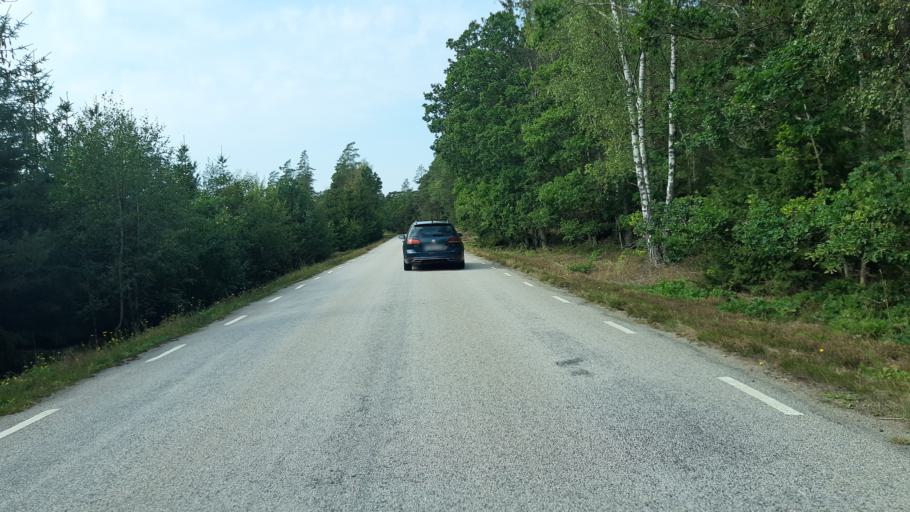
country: SE
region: Blekinge
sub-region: Ronneby Kommun
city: Kallinge
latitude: 56.2208
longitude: 15.3945
